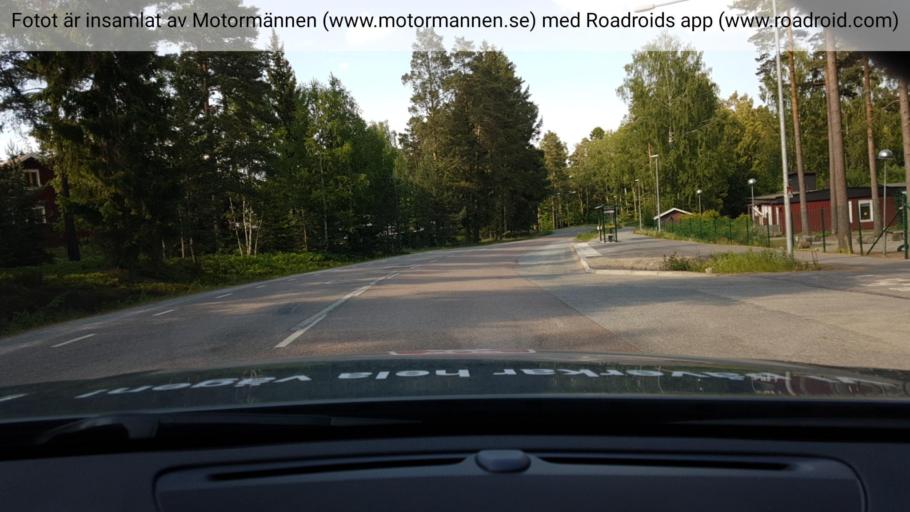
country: SE
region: Stockholm
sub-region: Varmdo Kommun
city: Mortnas
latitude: 59.2777
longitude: 18.4259
